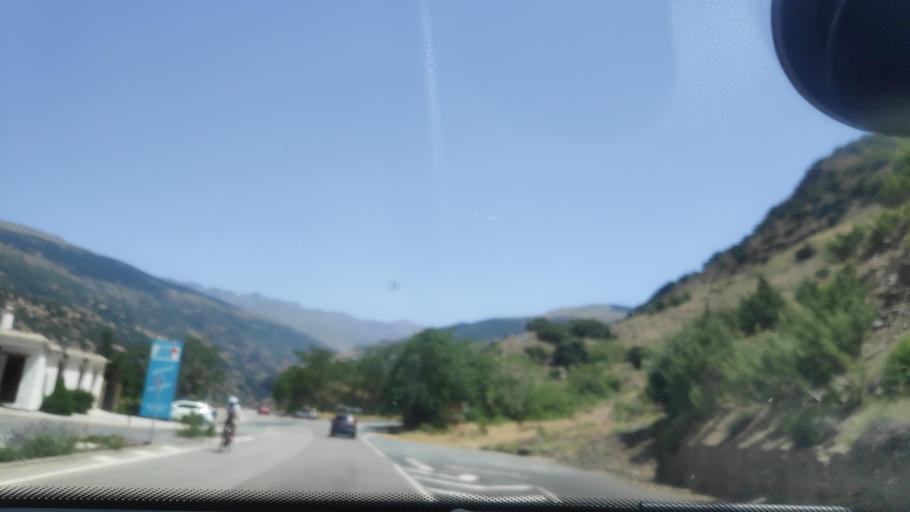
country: ES
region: Andalusia
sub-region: Provincia de Granada
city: Pampaneira
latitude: 36.9293
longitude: -3.3645
